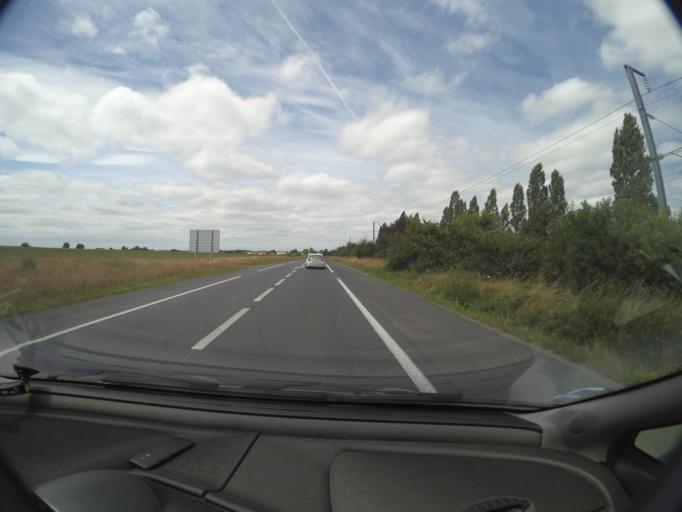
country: FR
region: Pays de la Loire
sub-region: Departement de la Loire-Atlantique
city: Gorges
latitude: 47.0958
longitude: -1.3003
